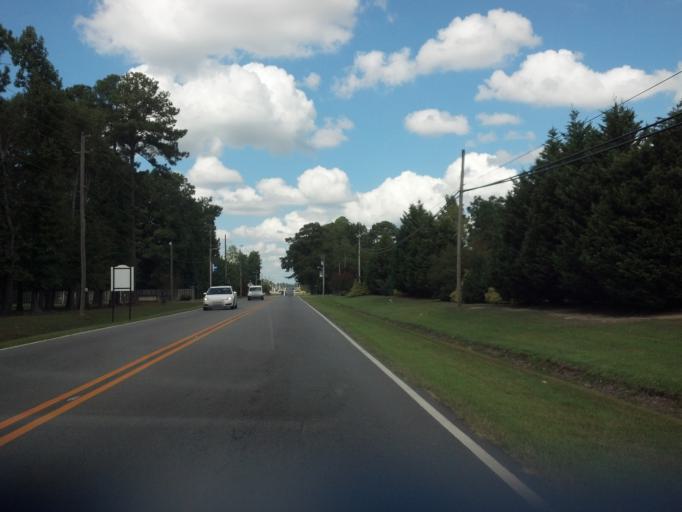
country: US
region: North Carolina
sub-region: Pitt County
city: Winterville
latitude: 35.5363
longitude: -77.4036
